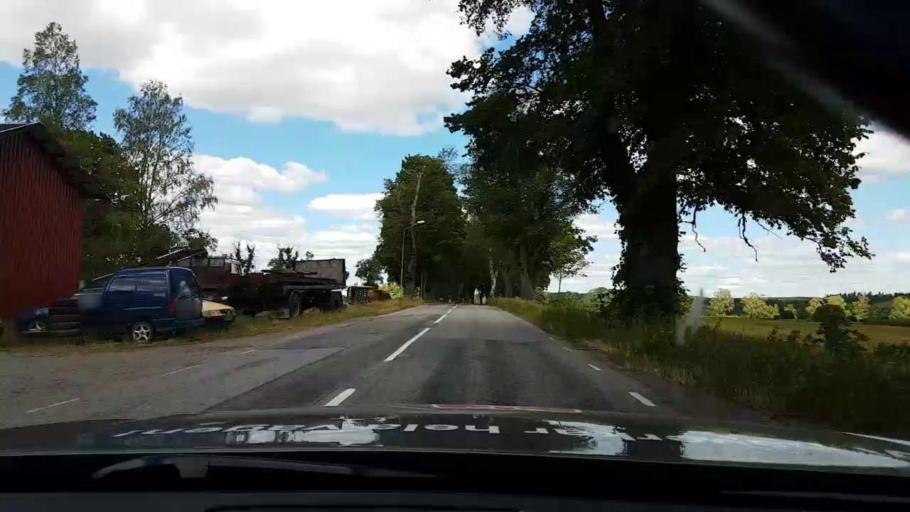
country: SE
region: Kalmar
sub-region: Vasterviks Kommun
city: Forserum
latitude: 58.0058
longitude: 16.4857
